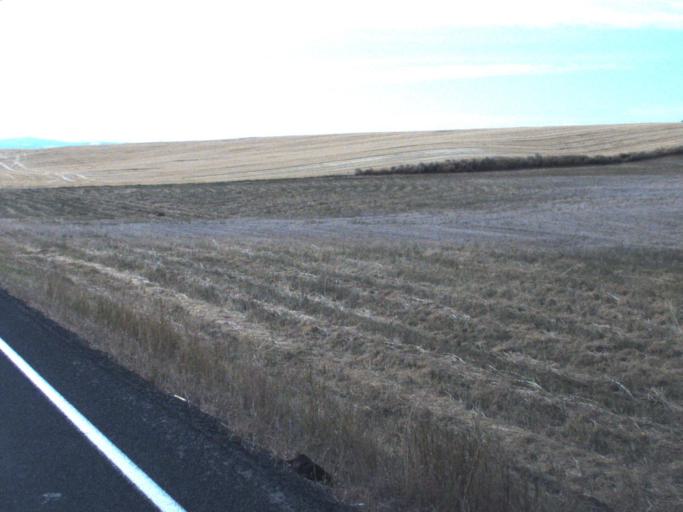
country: US
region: Washington
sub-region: Spokane County
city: Mead
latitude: 47.7875
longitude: -117.2811
